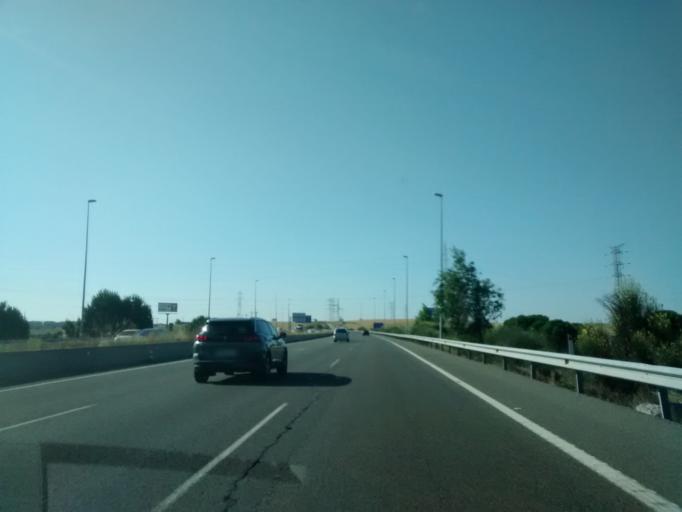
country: ES
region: Madrid
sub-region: Provincia de Madrid
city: Majadahonda
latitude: 40.4720
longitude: -3.8936
